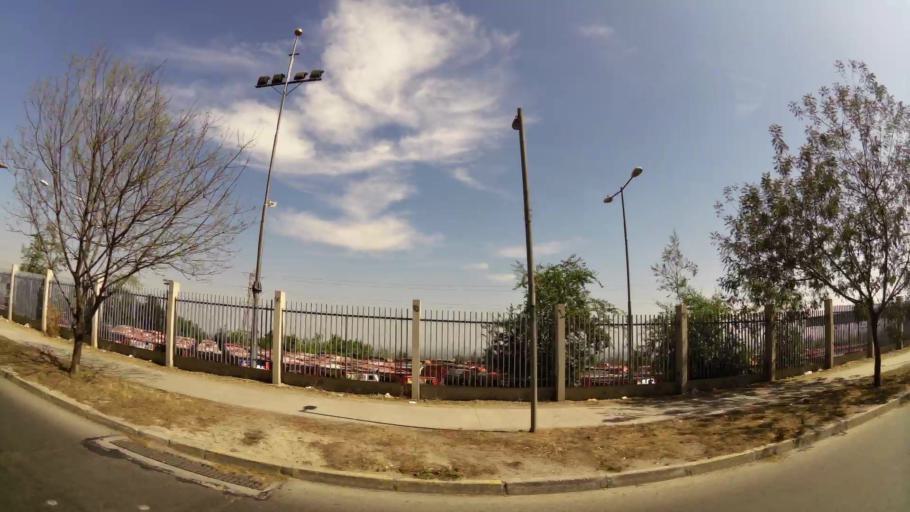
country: CL
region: Santiago Metropolitan
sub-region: Provincia de Santiago
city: Villa Presidente Frei, Nunoa, Santiago, Chile
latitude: -33.4641
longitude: -70.5308
